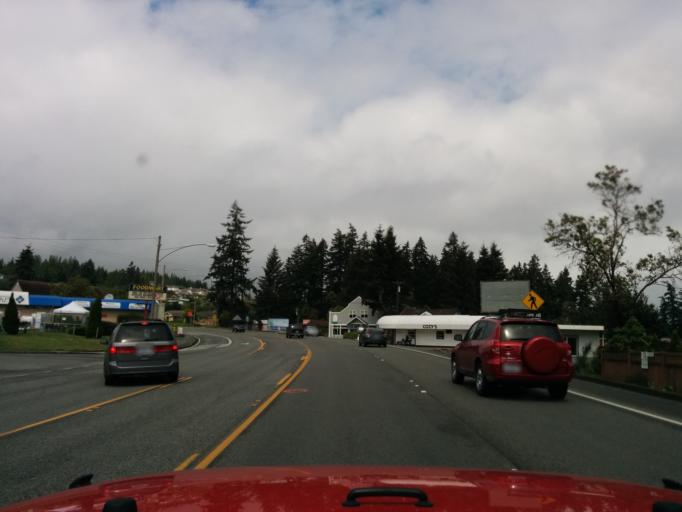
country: US
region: Washington
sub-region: Snohomish County
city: Mukilteo
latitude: 47.9787
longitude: -122.3562
